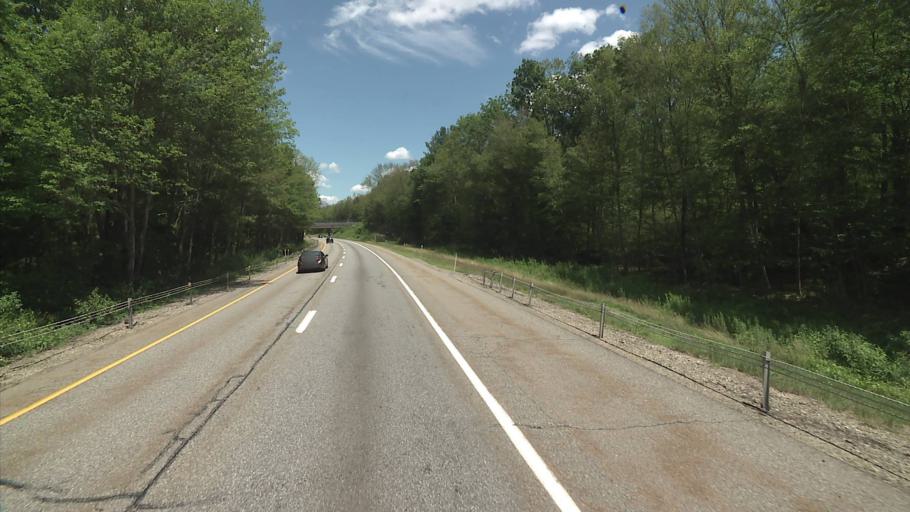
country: US
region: Connecticut
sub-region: Windham County
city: Thompson
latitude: 41.9798
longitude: -71.8564
